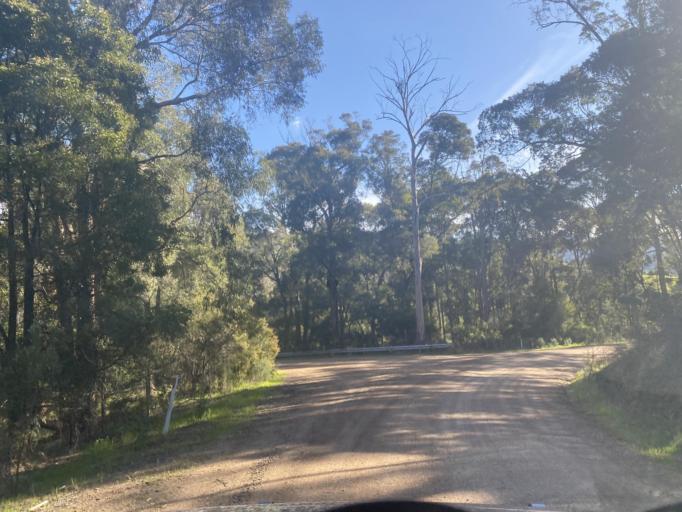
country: AU
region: Victoria
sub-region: Mansfield
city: Mansfield
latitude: -36.8273
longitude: 146.1438
